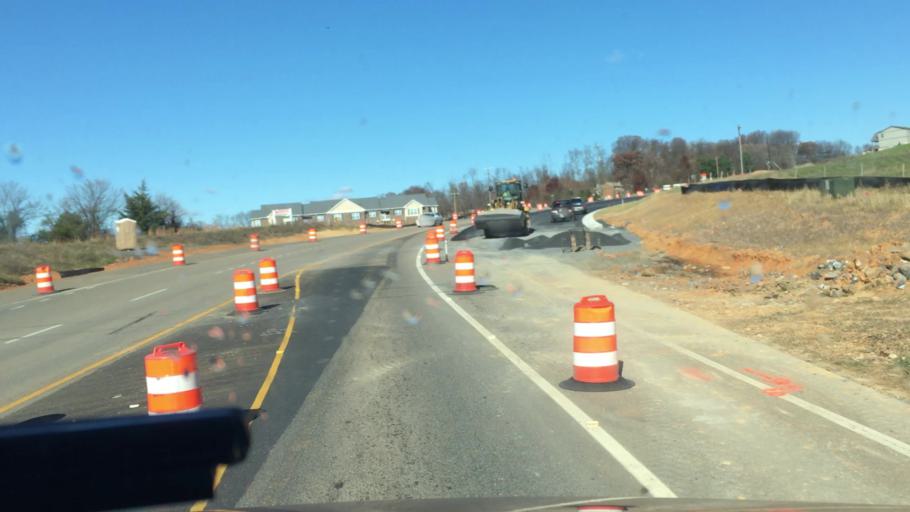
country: US
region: Virginia
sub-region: Rockingham County
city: Massanetta Springs
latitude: 38.4097
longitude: -78.8558
